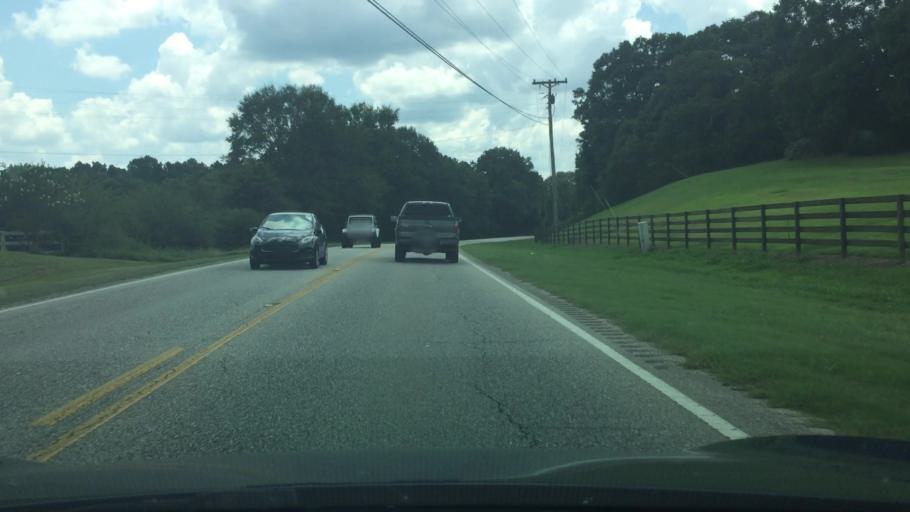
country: US
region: Alabama
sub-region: Pike County
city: Troy
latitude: 31.7404
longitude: -85.9574
